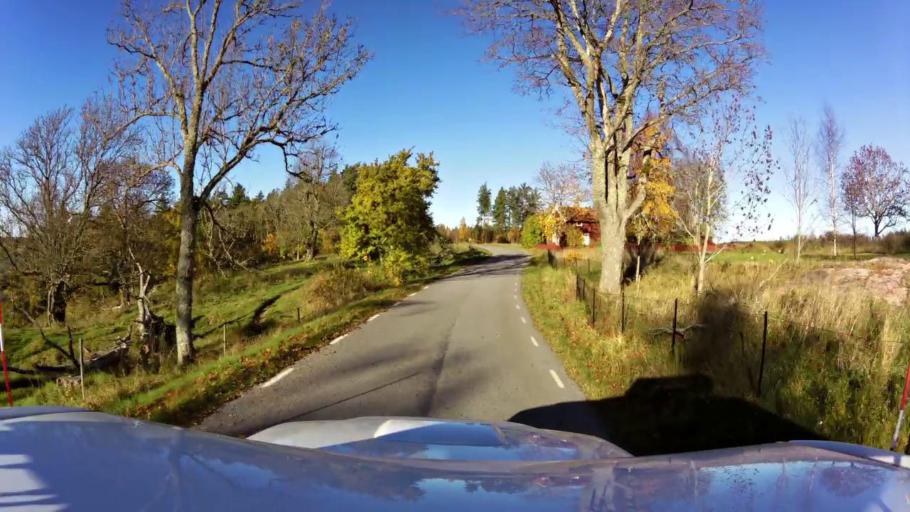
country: SE
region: OEstergoetland
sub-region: Linkopings Kommun
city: Ljungsbro
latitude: 58.5352
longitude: 15.4389
